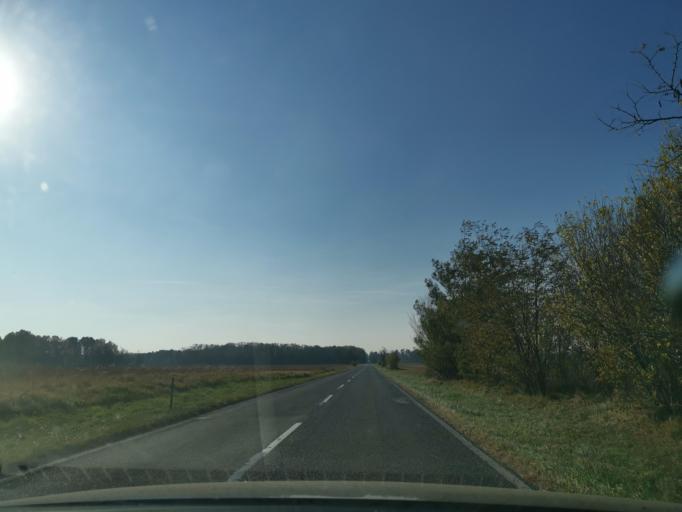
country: SK
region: Trnavsky
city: Gbely
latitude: 48.5766
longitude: 17.1751
